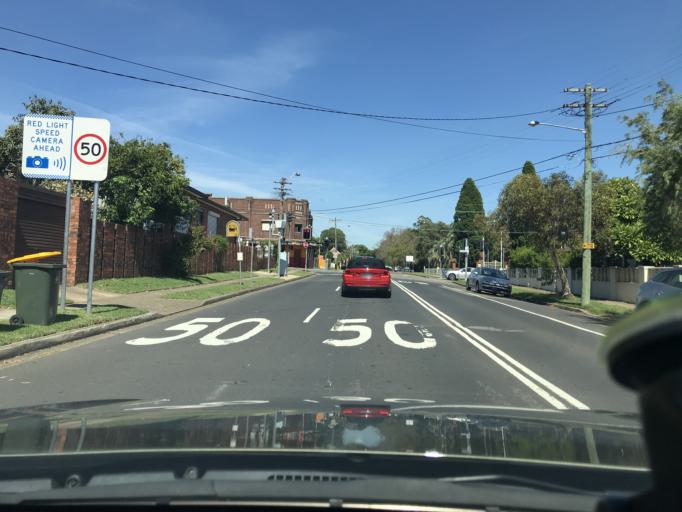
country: AU
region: New South Wales
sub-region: Canada Bay
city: Concord
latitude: -33.8611
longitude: 151.1064
